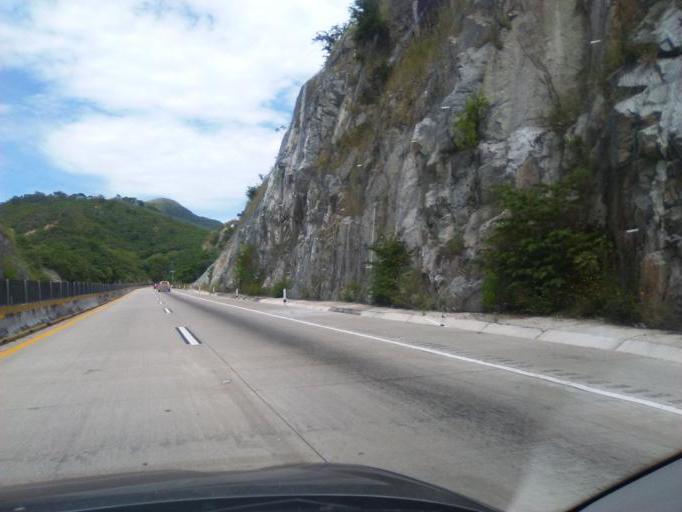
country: MX
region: Guerrero
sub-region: Chilpancingo de los Bravo
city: Julian Blanco (Dos Caminos)
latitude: 17.2075
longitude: -99.5377
